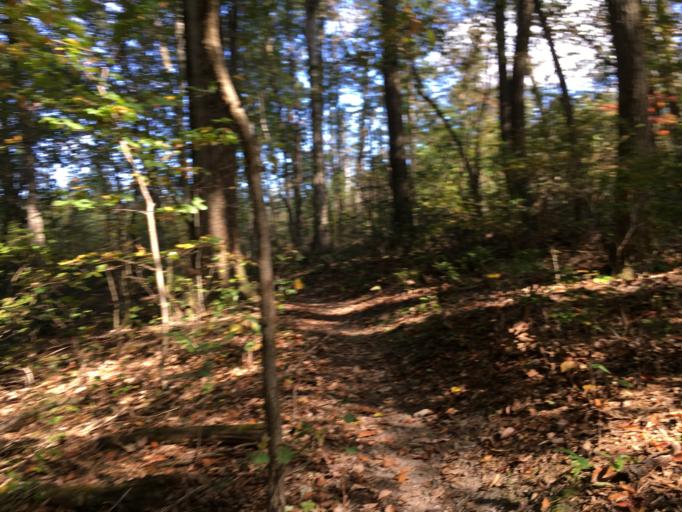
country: US
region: Pennsylvania
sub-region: York County
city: Yorklyn
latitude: 40.0105
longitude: -76.6512
